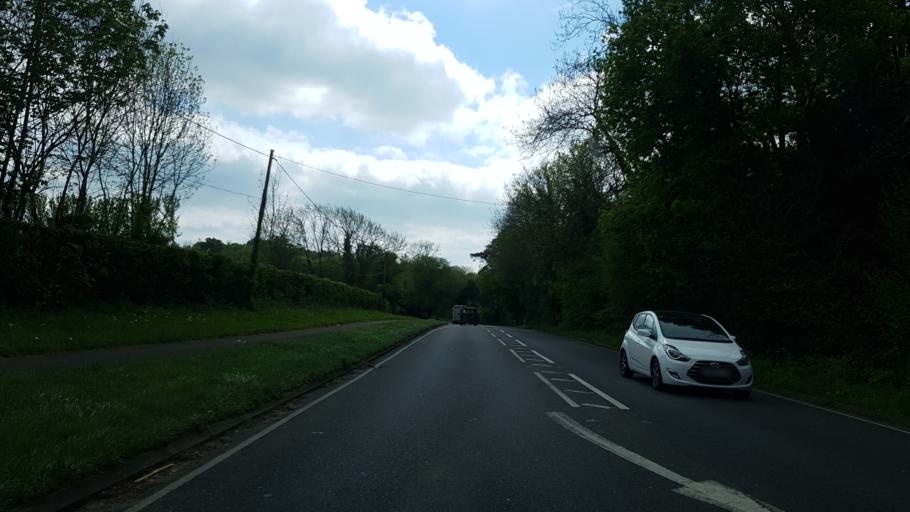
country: GB
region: England
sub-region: East Sussex
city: Robertsbridge
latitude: 51.0444
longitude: 0.4468
